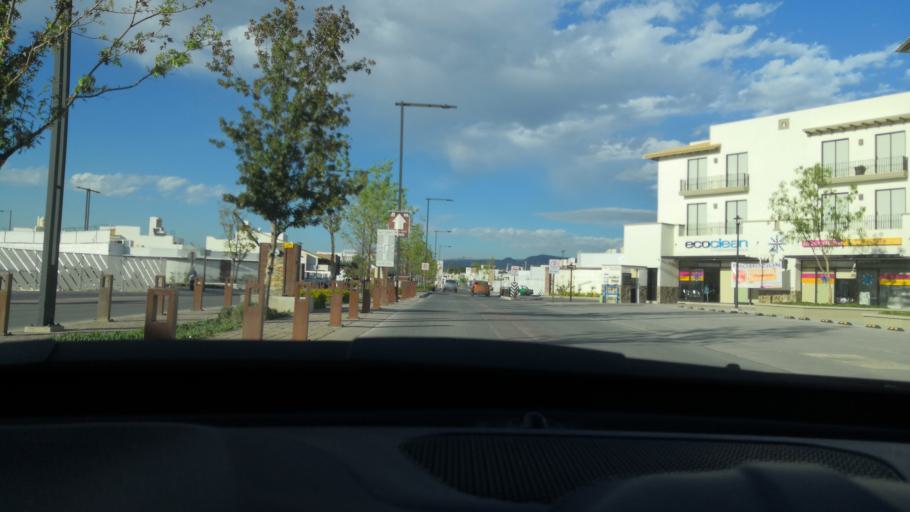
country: MX
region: Guanajuato
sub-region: Leon
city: San Jose de Duran (Los Troncoso)
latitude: 21.0862
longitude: -101.6531
